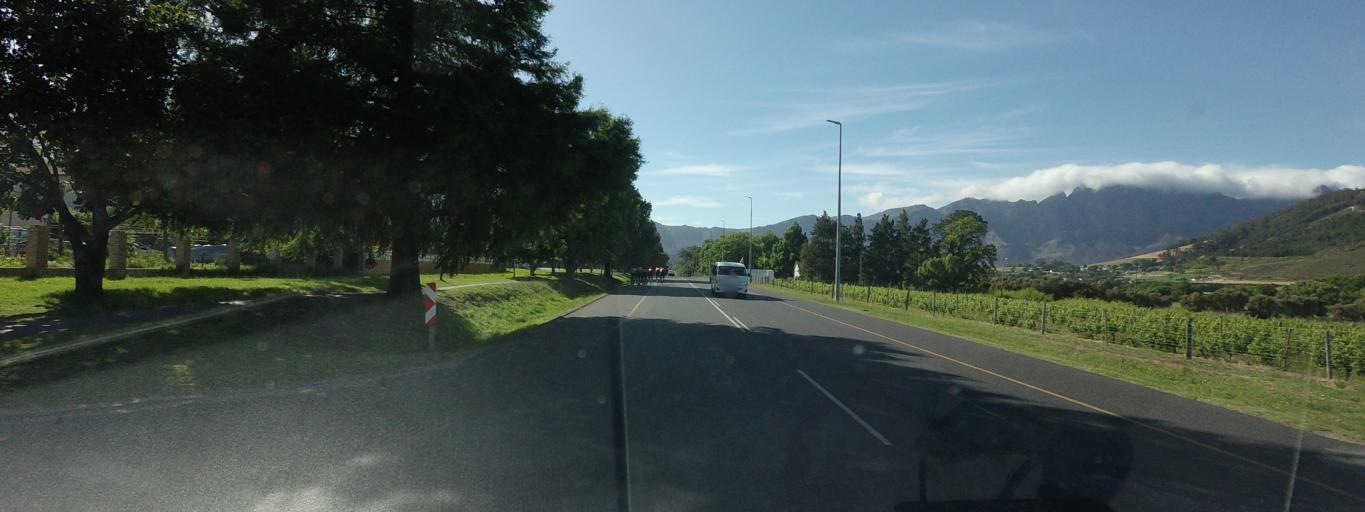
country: ZA
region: Western Cape
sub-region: Cape Winelands District Municipality
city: Paarl
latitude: -33.8973
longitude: 19.1019
